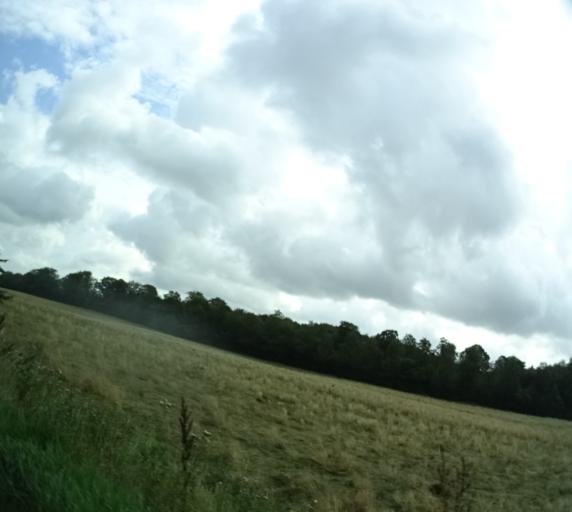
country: DK
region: Central Jutland
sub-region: Syddjurs Kommune
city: Ryomgard
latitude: 56.3993
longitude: 10.5184
